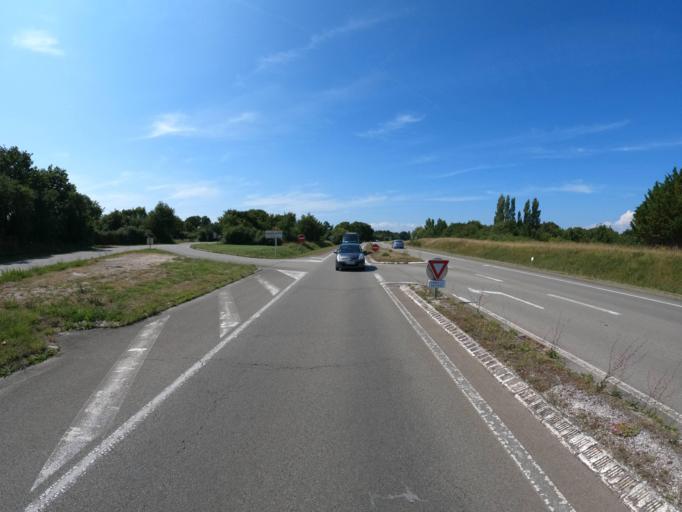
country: FR
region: Pays de la Loire
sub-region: Departement de la Loire-Atlantique
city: La Bernerie-en-Retz
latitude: 47.0908
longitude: -2.0330
